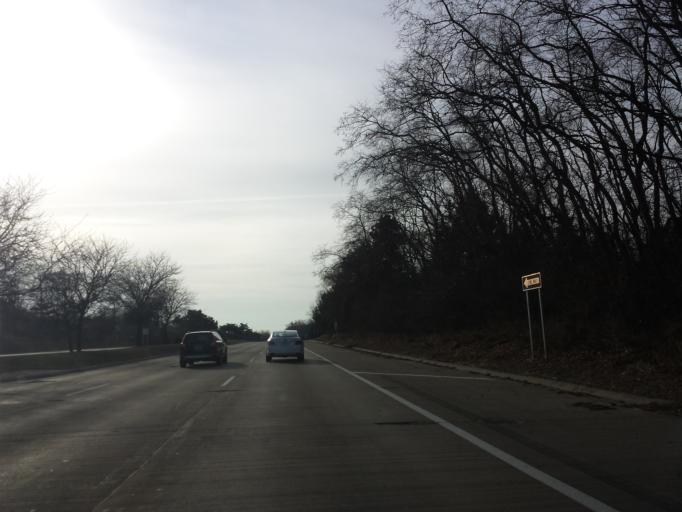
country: US
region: Michigan
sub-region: Oakland County
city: Bloomfield Hills
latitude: 42.5907
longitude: -83.2817
